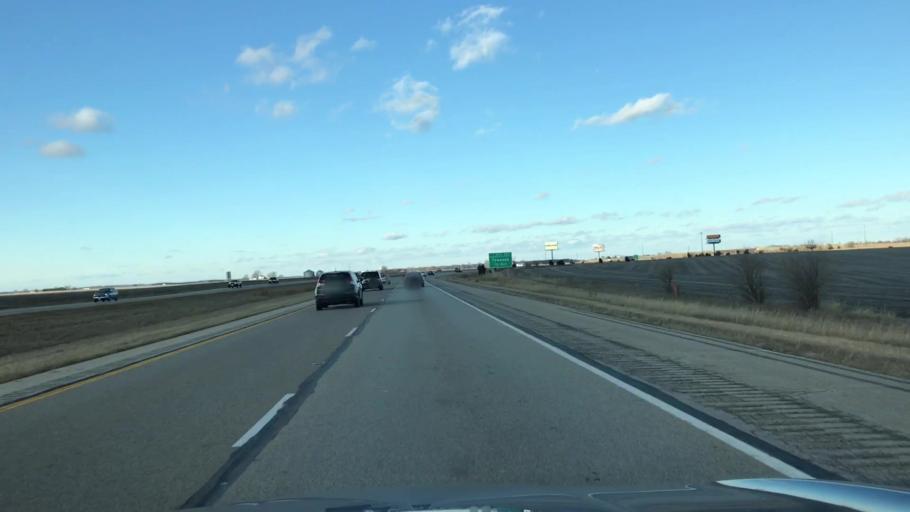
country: US
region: Illinois
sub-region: McLean County
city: Hudson
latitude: 40.5619
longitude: -88.9085
